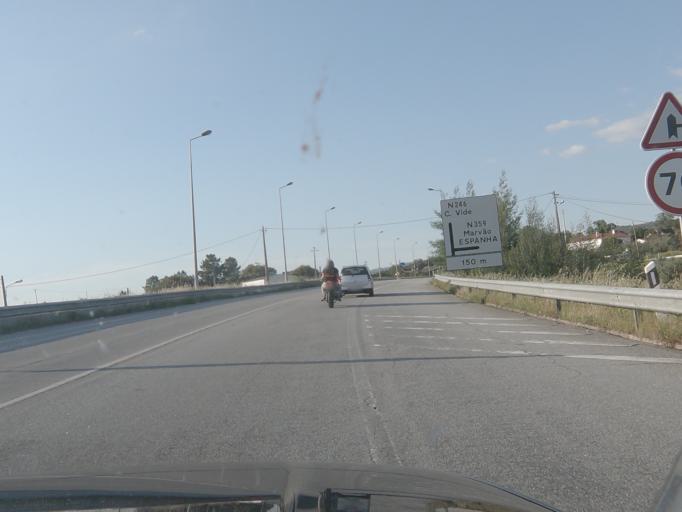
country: PT
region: Portalegre
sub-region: Portalegre
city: Portalegre
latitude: 39.3092
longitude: -7.4430
